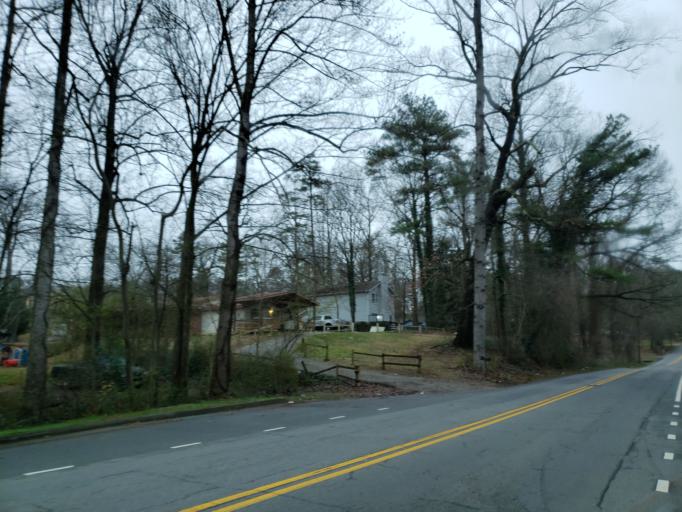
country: US
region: Georgia
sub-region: Cobb County
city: Fair Oaks
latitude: 33.9012
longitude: -84.5307
